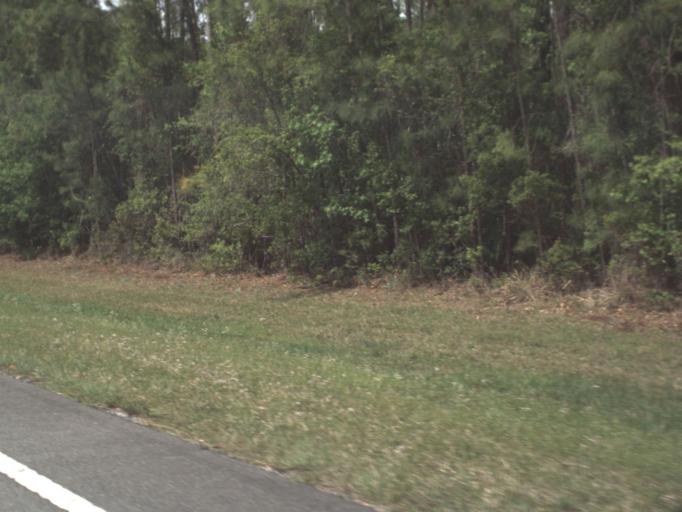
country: US
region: Florida
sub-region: Putnam County
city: Crescent City
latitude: 29.5164
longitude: -81.5025
